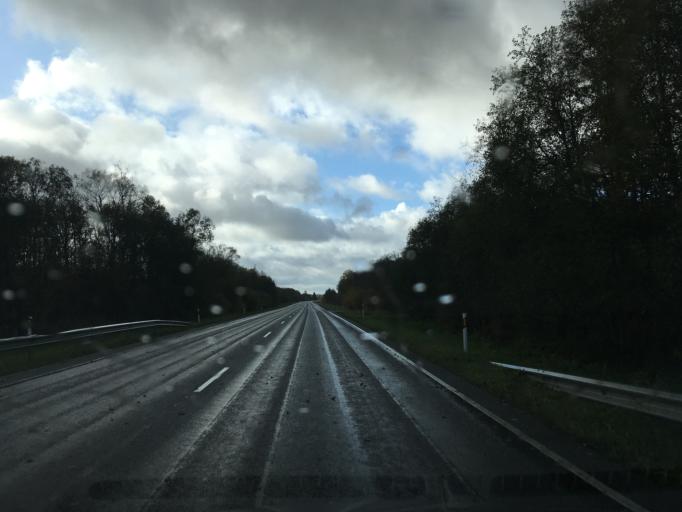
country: EE
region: Laeaene
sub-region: Lihula vald
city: Lihula
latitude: 58.6926
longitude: 23.8184
